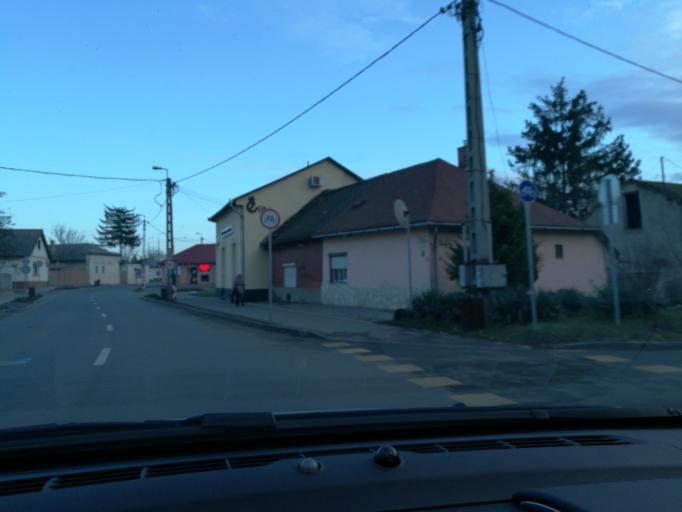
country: HU
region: Szabolcs-Szatmar-Bereg
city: Nyiregyhaza
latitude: 47.9475
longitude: 21.7171
